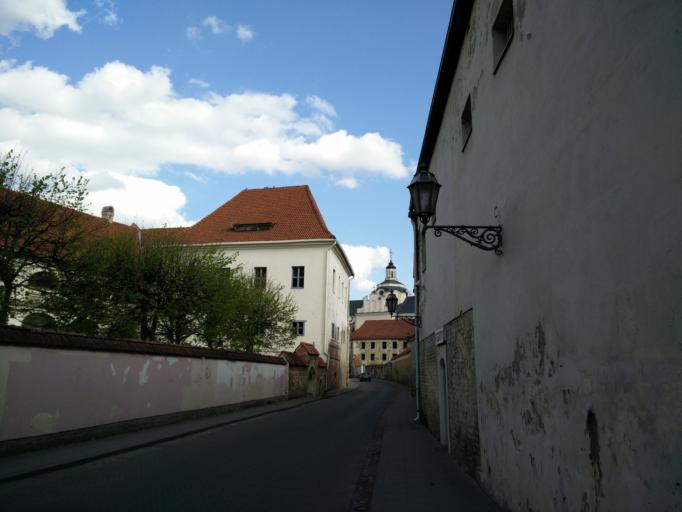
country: LT
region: Vilnius County
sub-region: Vilnius
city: Vilnius
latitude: 54.6824
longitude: 25.2819
